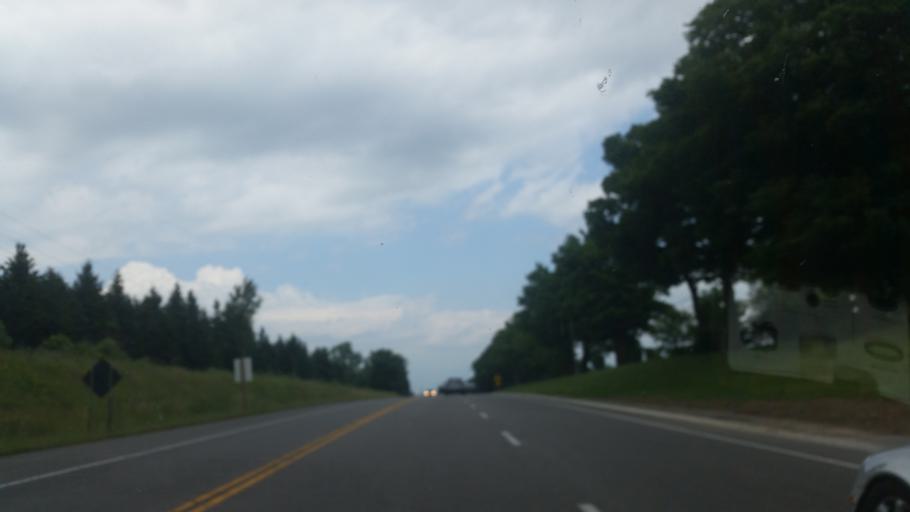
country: CA
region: Ontario
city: Orangeville
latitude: 43.7116
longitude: -80.1192
